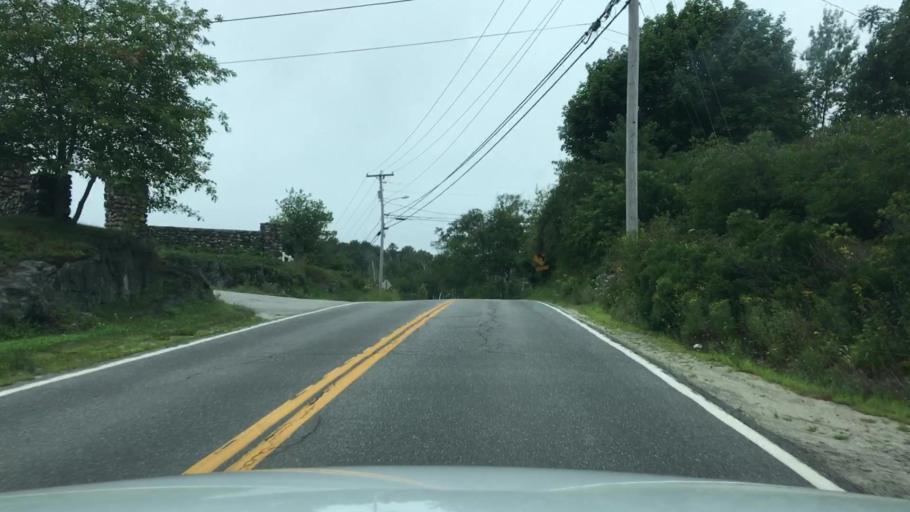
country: US
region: Maine
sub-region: Cumberland County
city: Harpswell Center
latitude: 43.7735
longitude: -69.9648
